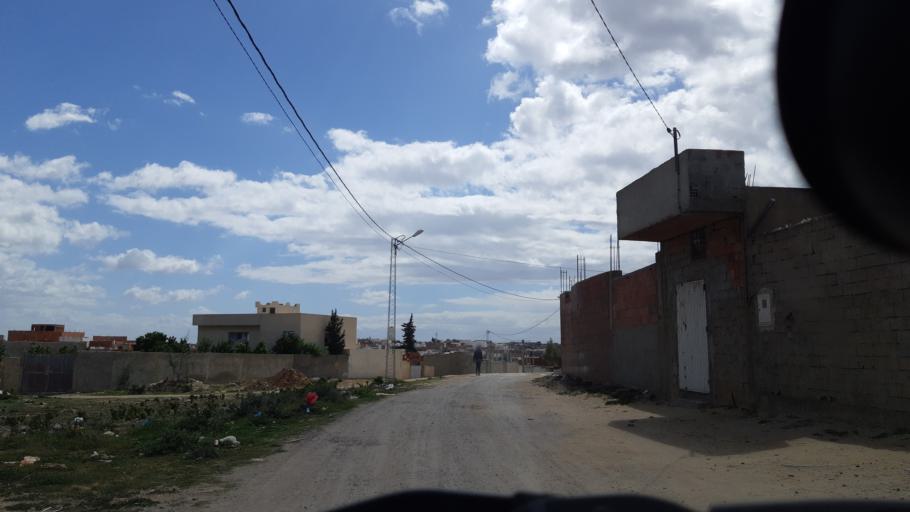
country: TN
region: Susah
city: Akouda
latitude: 35.8782
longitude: 10.5192
